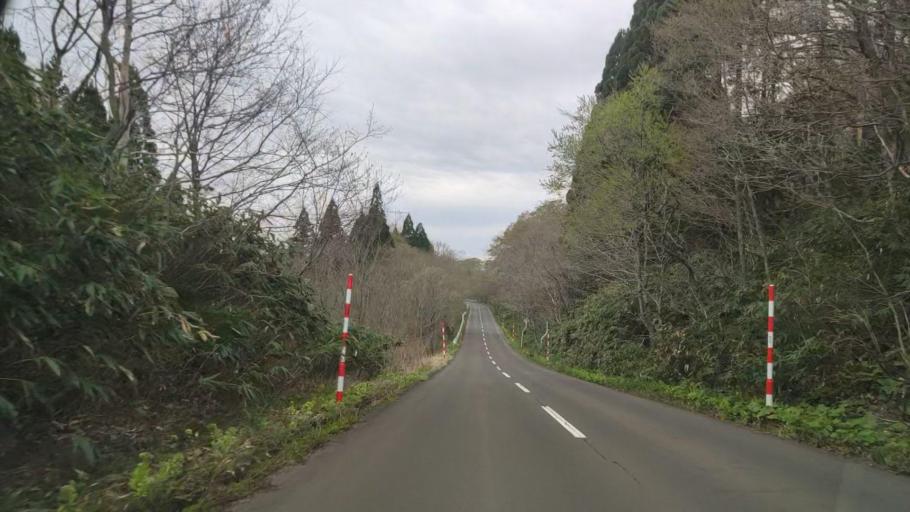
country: JP
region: Akita
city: Hanawa
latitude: 40.4082
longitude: 140.8151
